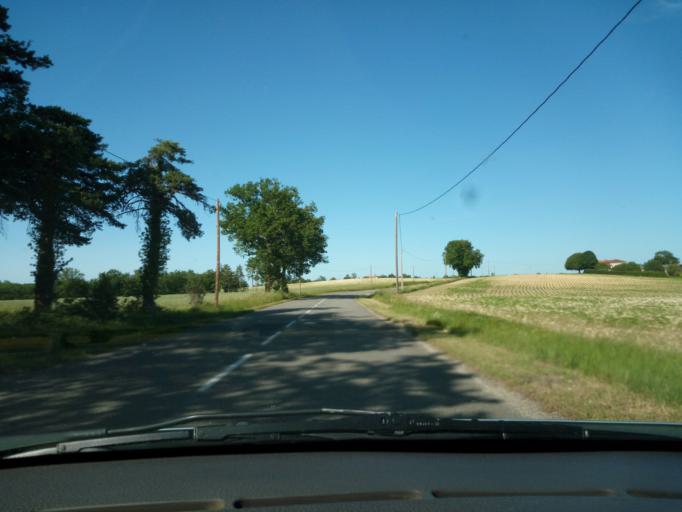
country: FR
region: Midi-Pyrenees
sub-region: Departement du Lot
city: Castelnau-Montratier
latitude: 44.3008
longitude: 1.4090
